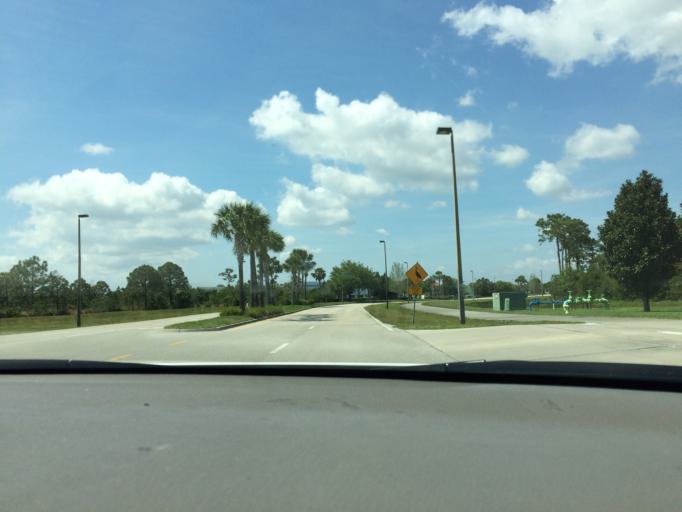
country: US
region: Florida
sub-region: Sarasota County
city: The Meadows
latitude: 27.3782
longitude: -82.4234
